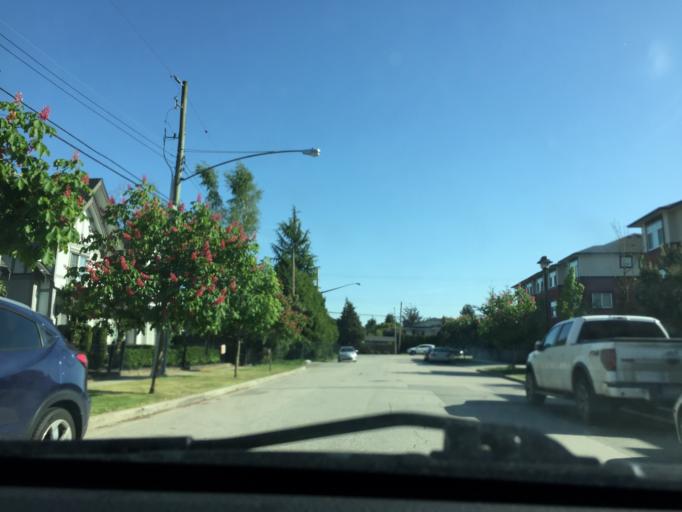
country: CA
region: British Columbia
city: Richmond
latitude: 49.1564
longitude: -123.1170
